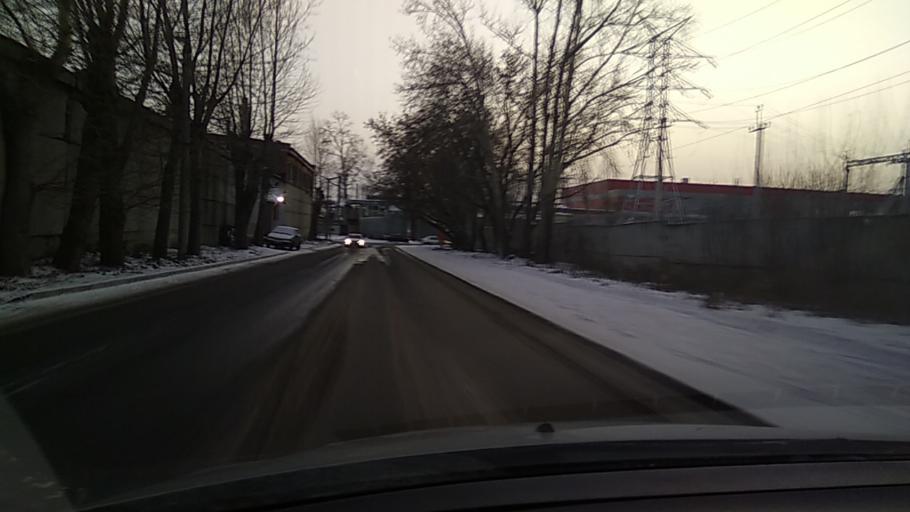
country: RU
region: Sverdlovsk
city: Istok
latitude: 56.7597
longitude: 60.7165
